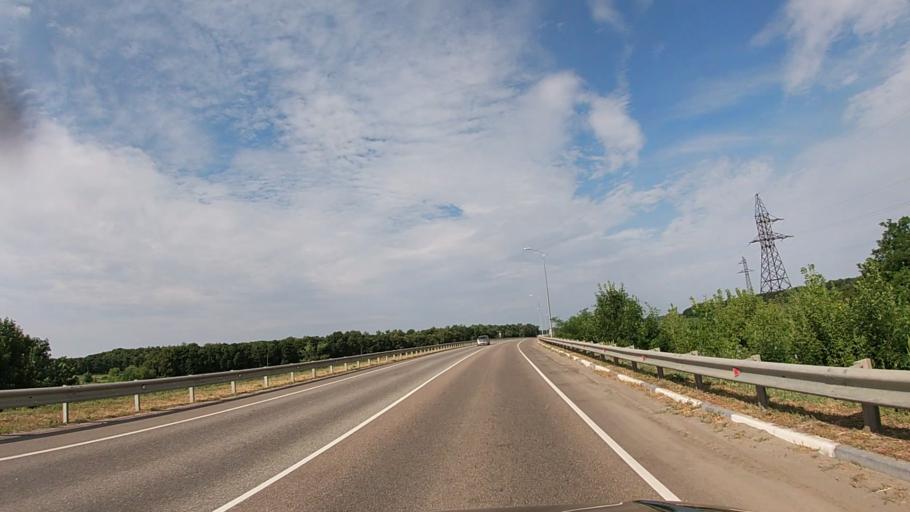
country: RU
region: Belgorod
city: Proletarskiy
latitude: 50.8032
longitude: 35.7371
